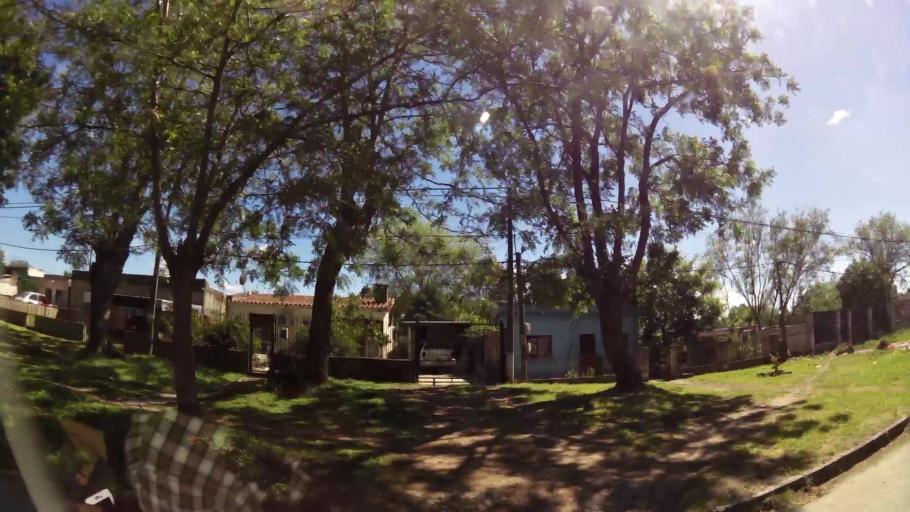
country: UY
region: Canelones
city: Paso de Carrasco
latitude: -34.8452
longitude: -56.1163
